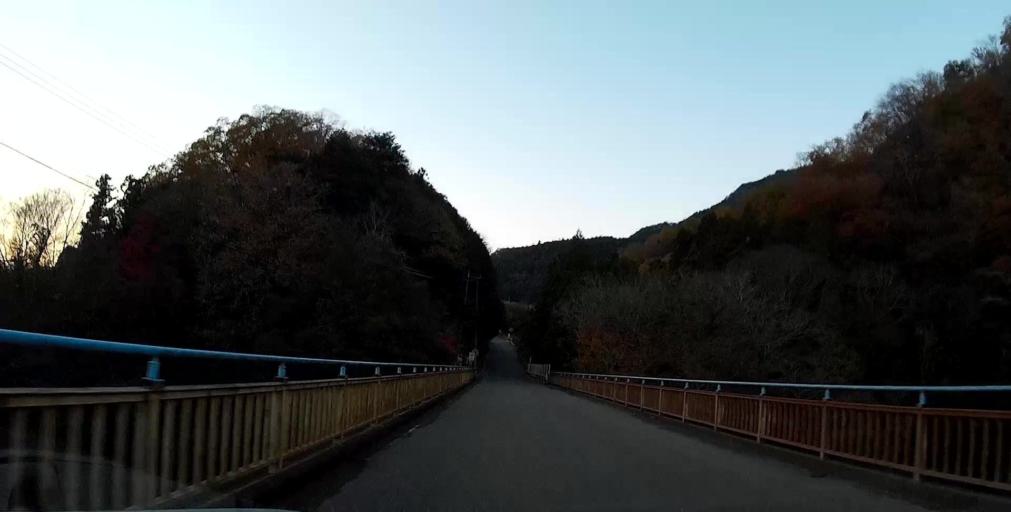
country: JP
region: Yamanashi
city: Uenohara
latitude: 35.5684
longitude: 139.2048
